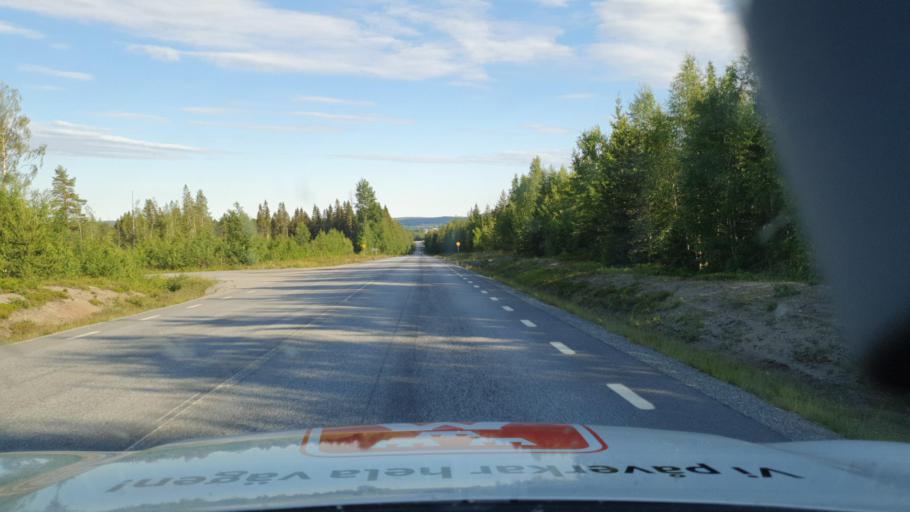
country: SE
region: Vaesterbotten
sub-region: Vannas Kommun
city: Vannasby
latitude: 64.0439
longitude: 20.0030
